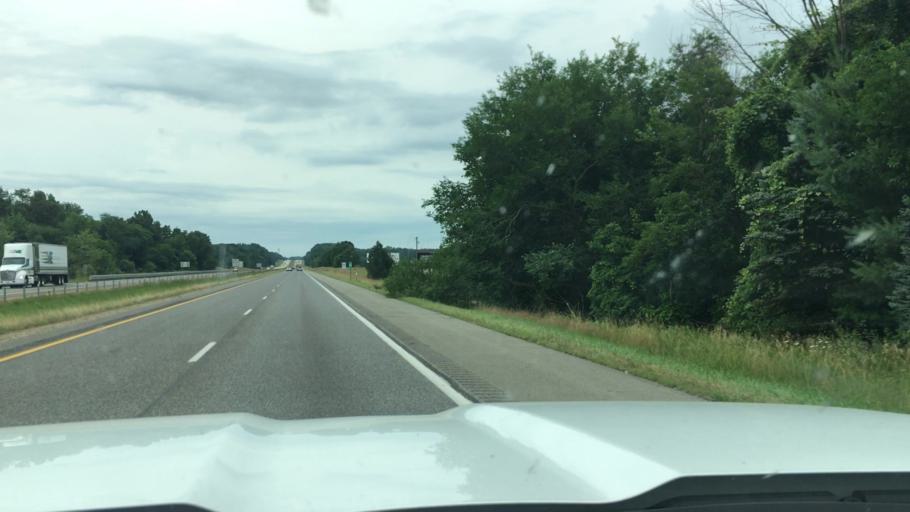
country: US
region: Michigan
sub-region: Allegan County
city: Otsego
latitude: 42.5241
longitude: -85.6577
